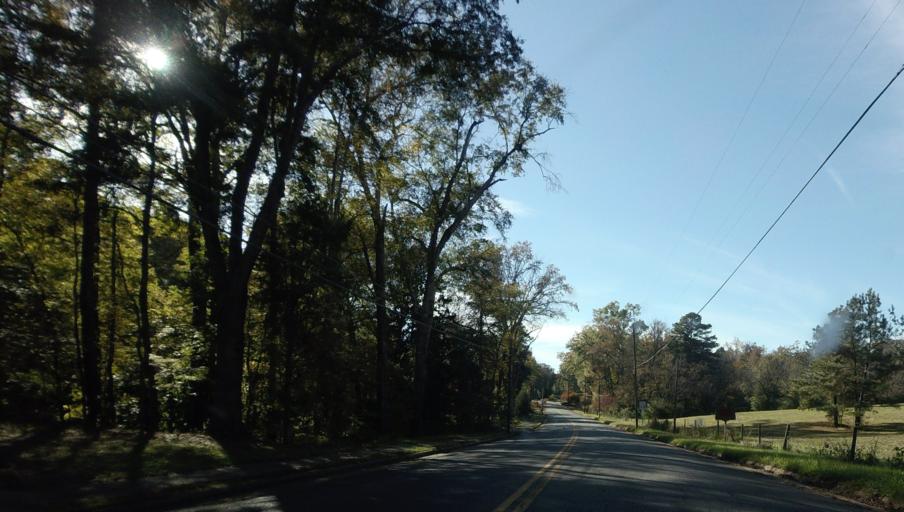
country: US
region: Georgia
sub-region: Talbot County
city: Talbotton
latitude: 32.6778
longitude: -84.5456
